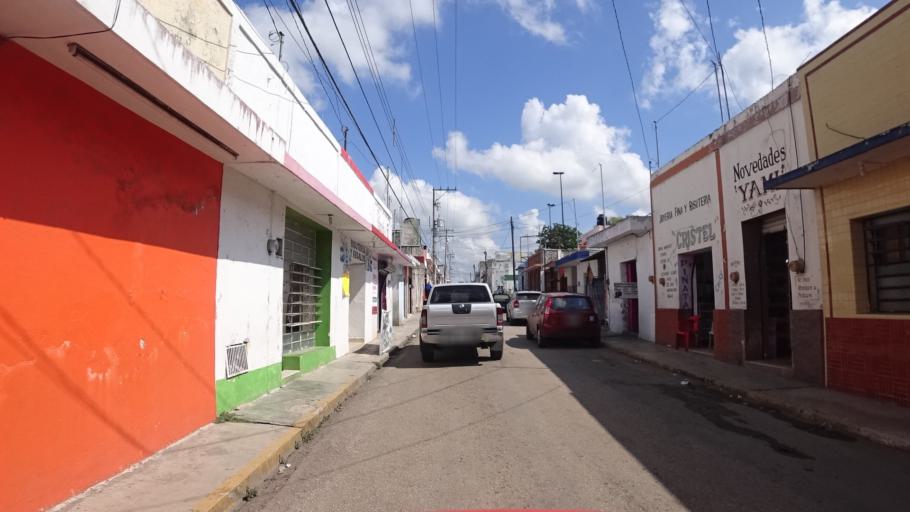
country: MX
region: Yucatan
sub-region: Tizimin
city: Tizimin
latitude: 21.1447
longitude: -88.1514
